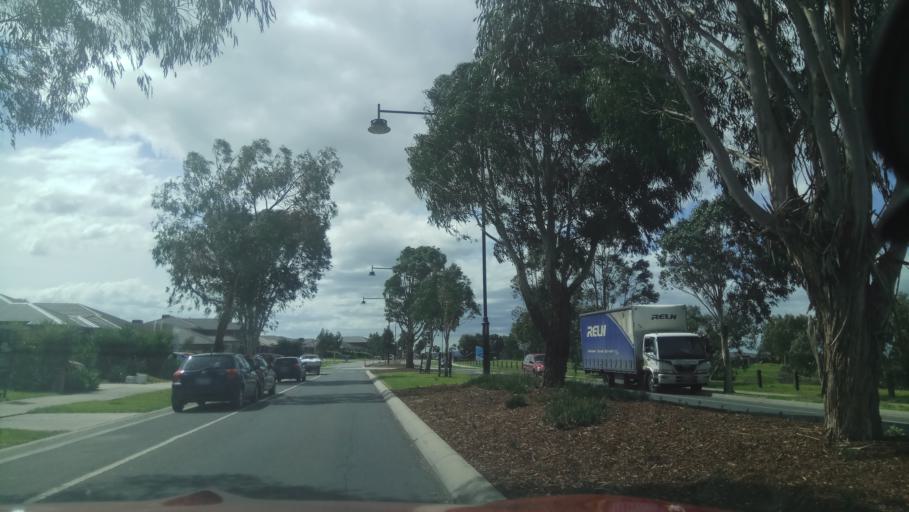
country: AU
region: Victoria
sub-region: Casey
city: Lynbrook
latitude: -38.0722
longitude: 145.2463
